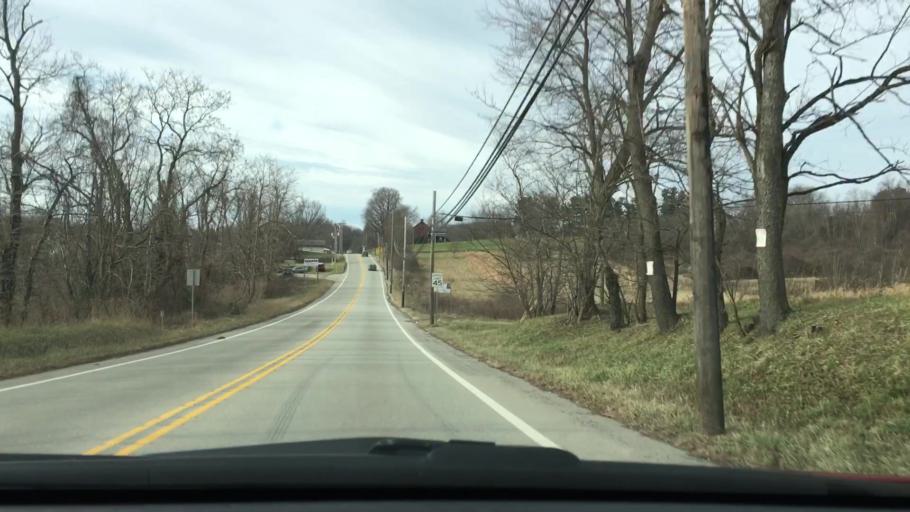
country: US
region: Pennsylvania
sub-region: Fayette County
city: South Uniontown
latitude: 39.8968
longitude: -79.7841
